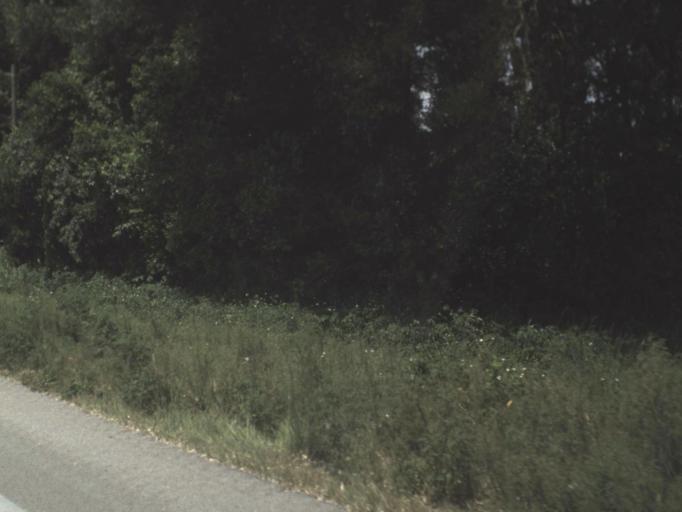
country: US
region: Florida
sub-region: Gilchrist County
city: Trenton
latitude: 29.7404
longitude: -82.8578
